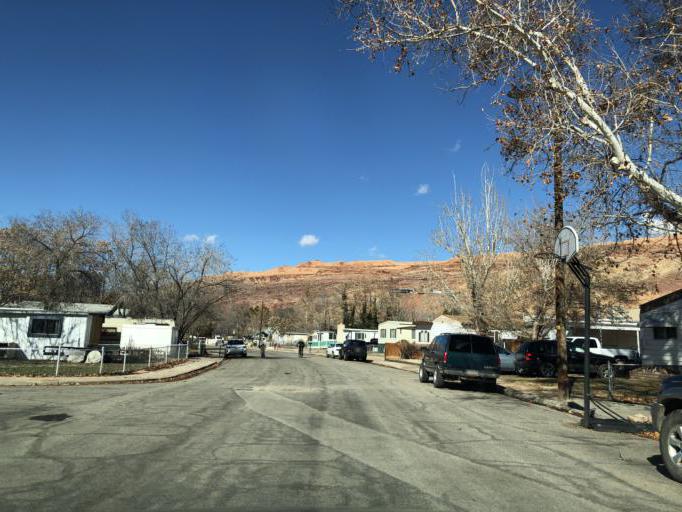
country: US
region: Utah
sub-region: Grand County
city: Moab
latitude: 38.5800
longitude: -109.5569
